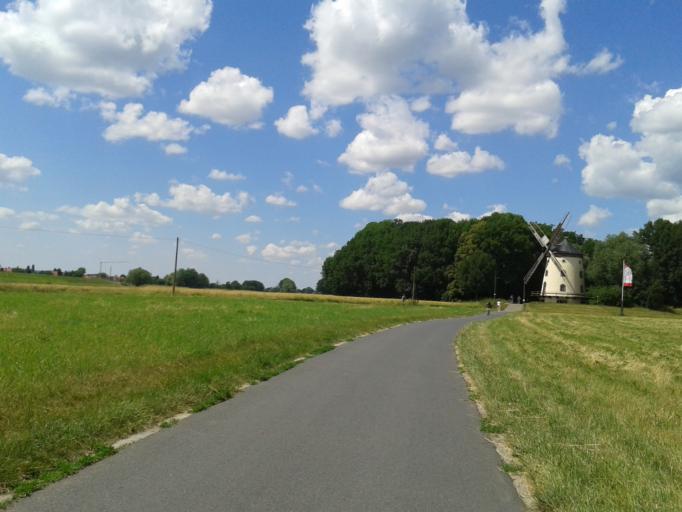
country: DE
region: Saxony
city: Radebeul
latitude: 51.0886
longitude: 13.6592
